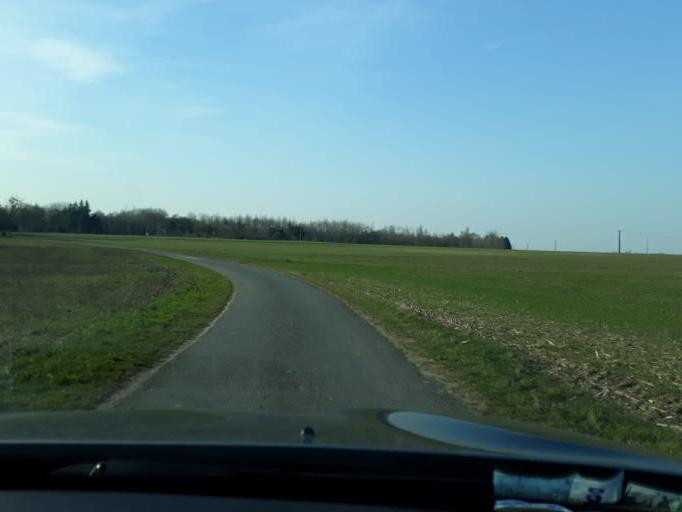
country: FR
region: Centre
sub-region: Departement du Loiret
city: Meung-sur-Loire
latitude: 47.8646
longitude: 1.6753
